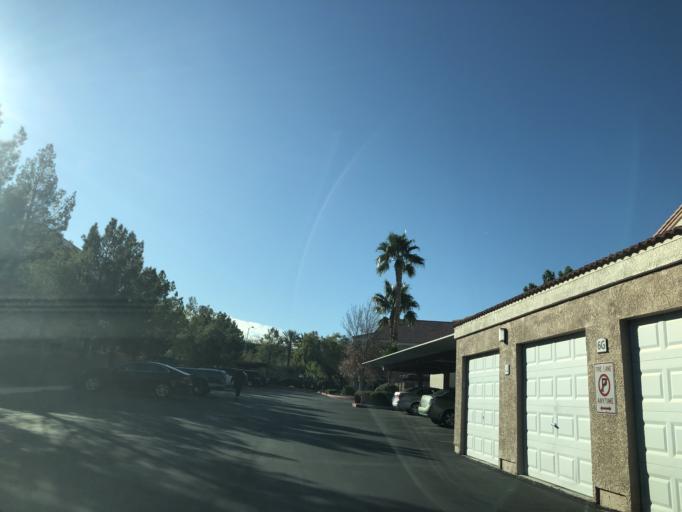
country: US
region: Nevada
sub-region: Clark County
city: Whitney
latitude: 36.0016
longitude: -115.0925
